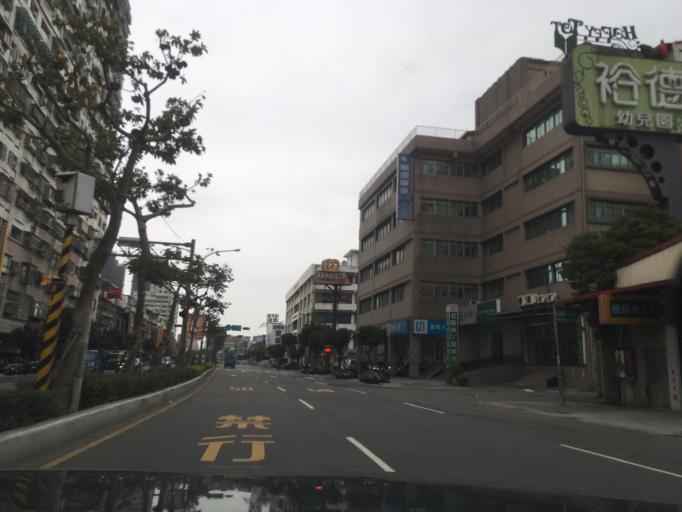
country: TW
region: Taipei
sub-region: Taipei
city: Banqiao
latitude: 24.9892
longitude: 121.4464
